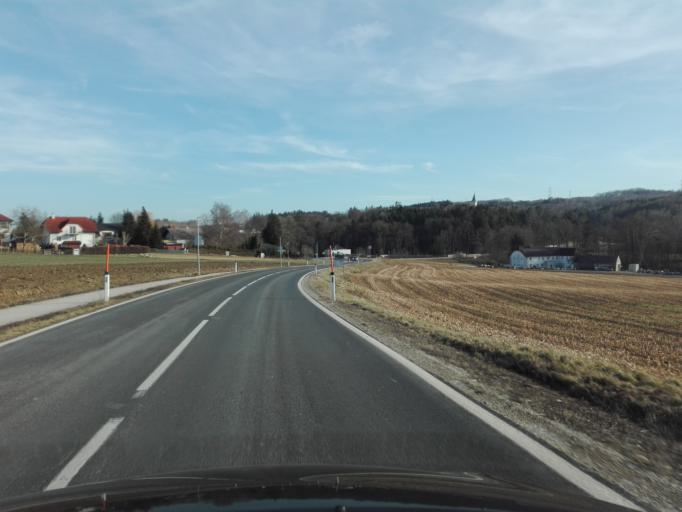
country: AT
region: Lower Austria
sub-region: Politischer Bezirk Amstetten
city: Amstetten
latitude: 48.1660
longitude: 14.8407
